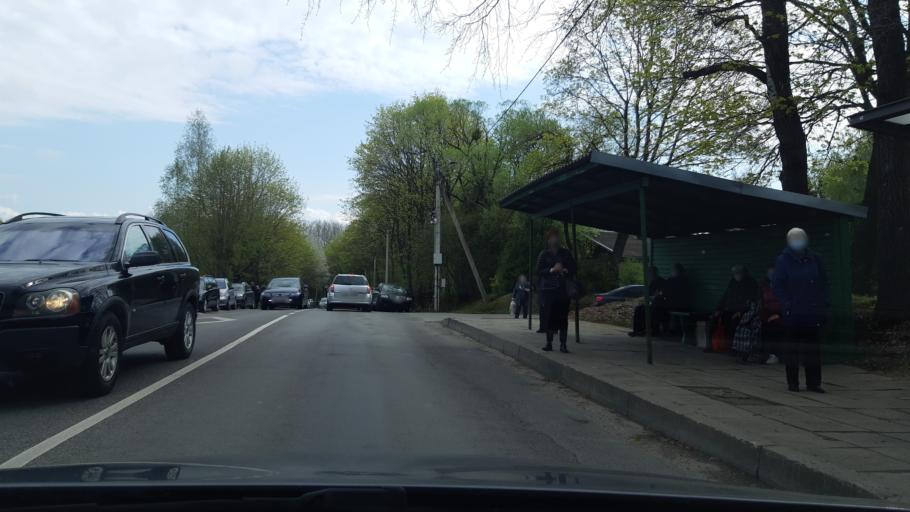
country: LT
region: Kauno apskritis
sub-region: Kaunas
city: Silainiai
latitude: 54.9242
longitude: 23.8549
